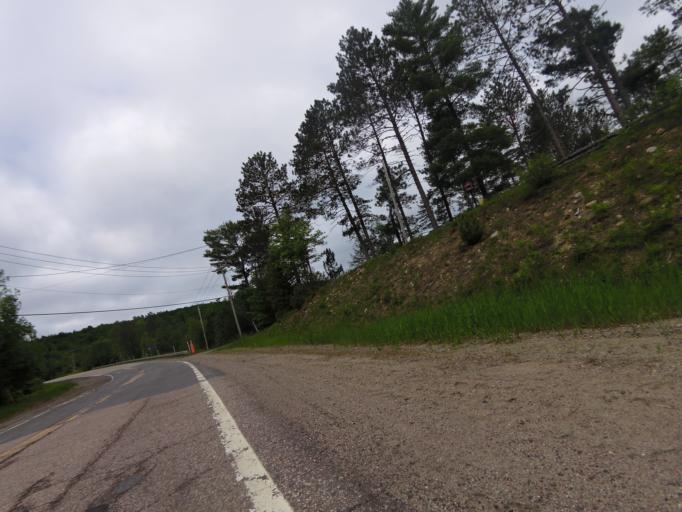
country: CA
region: Quebec
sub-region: Outaouais
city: Shawville
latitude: 45.8374
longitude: -76.4577
